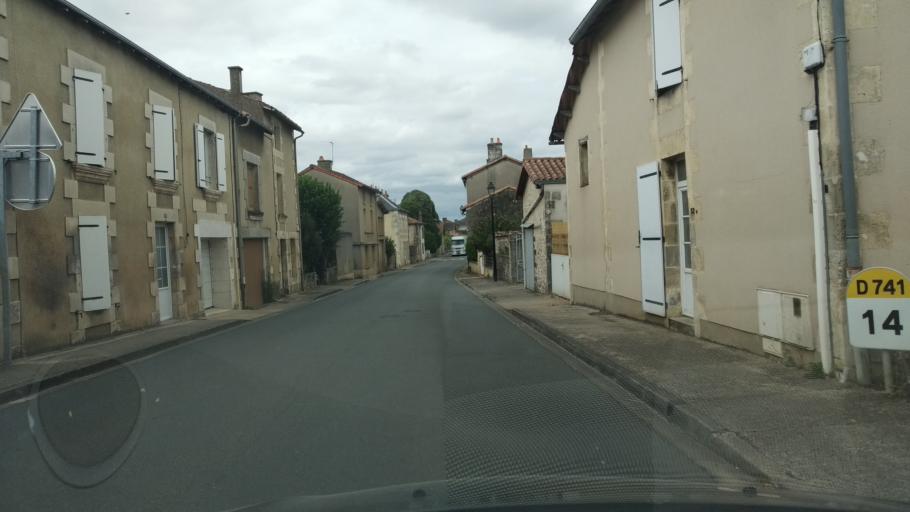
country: FR
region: Poitou-Charentes
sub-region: Departement de la Vienne
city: La Villedieu-du-Clain
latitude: 46.4534
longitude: 0.3670
